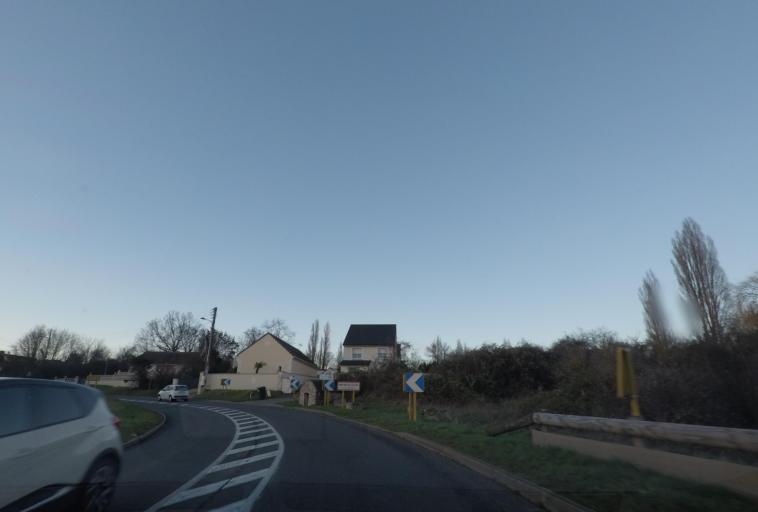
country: FR
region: Ile-de-France
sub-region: Departement de l'Essonne
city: Mennecy
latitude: 48.5817
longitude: 2.4374
